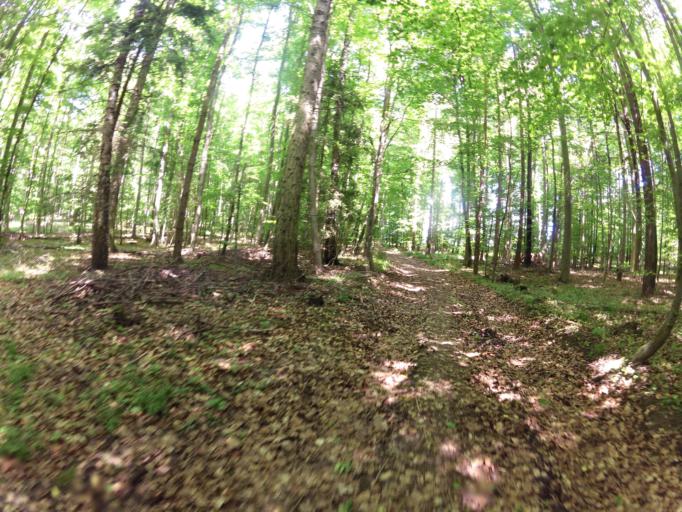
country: DE
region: Bavaria
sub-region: Regierungsbezirk Unterfranken
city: Uettingen
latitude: 49.7794
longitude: 9.7552
